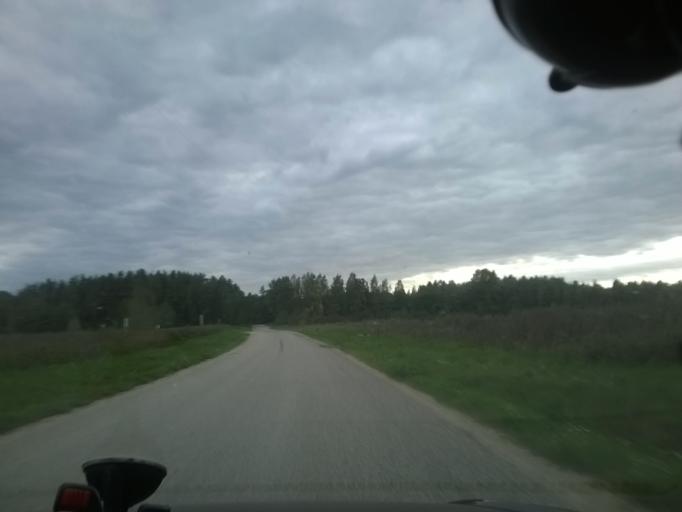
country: EE
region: Vorumaa
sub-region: Voru linn
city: Voru
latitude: 57.8196
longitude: 27.1205
